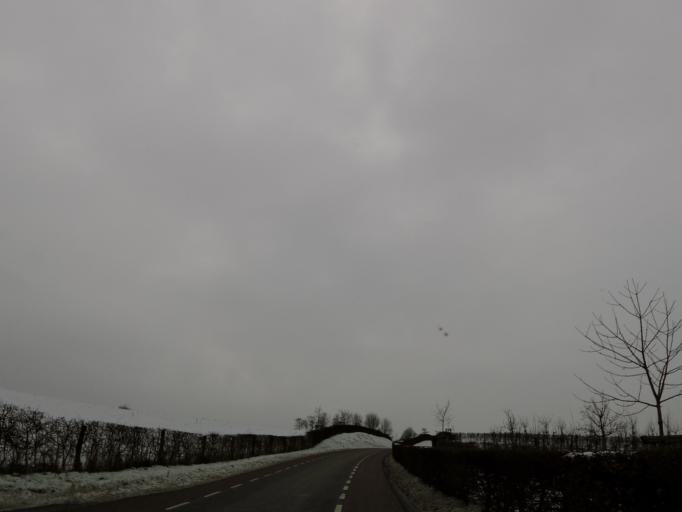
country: NL
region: Limburg
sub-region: Gemeente Voerendaal
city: Ubachsberg
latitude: 50.8221
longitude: 5.9233
